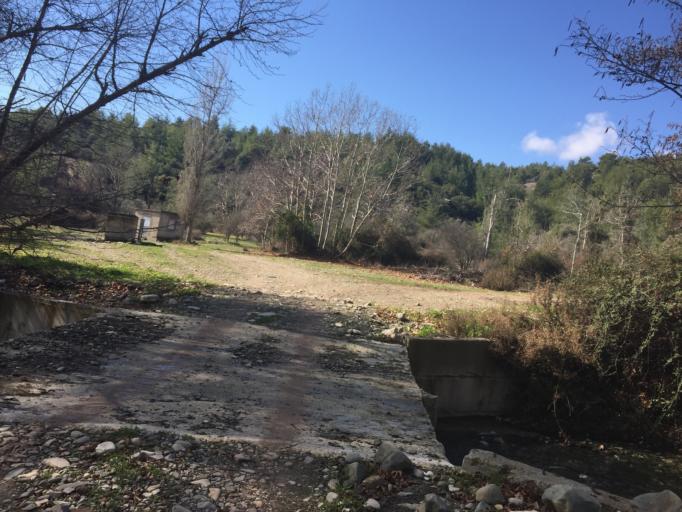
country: CY
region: Limassol
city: Pachna
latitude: 34.8816
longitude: 32.6768
